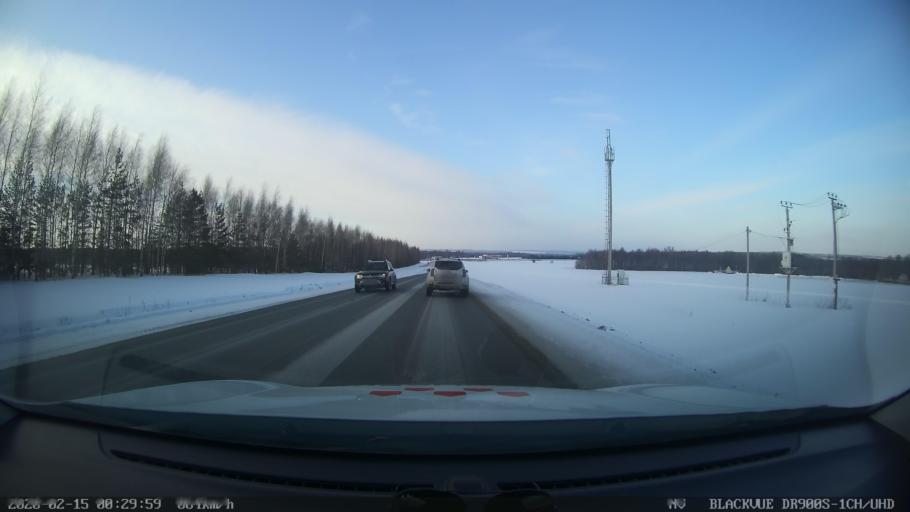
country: RU
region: Tatarstan
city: Verkhniy Uslon
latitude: 55.6553
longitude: 48.8625
